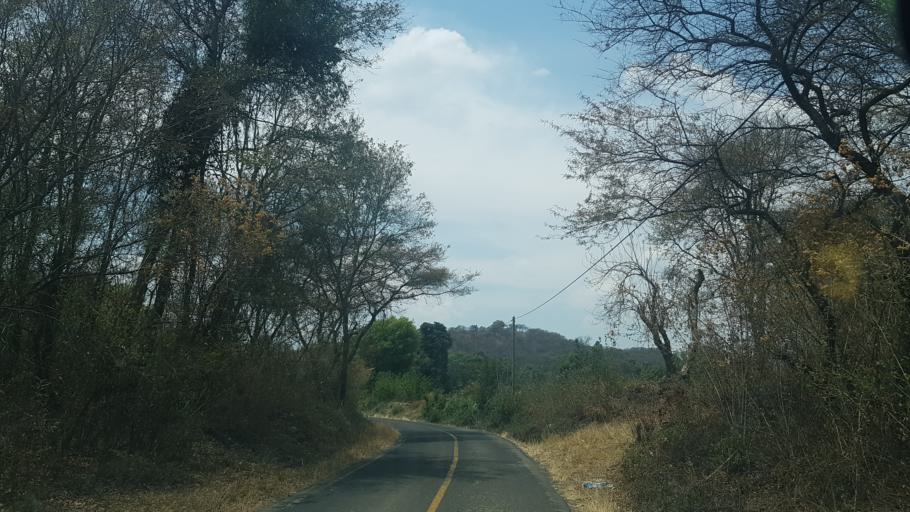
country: MX
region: Puebla
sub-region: Tochimilco
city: La Magdalena Yancuitlalpan
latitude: 18.8819
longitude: -98.5949
